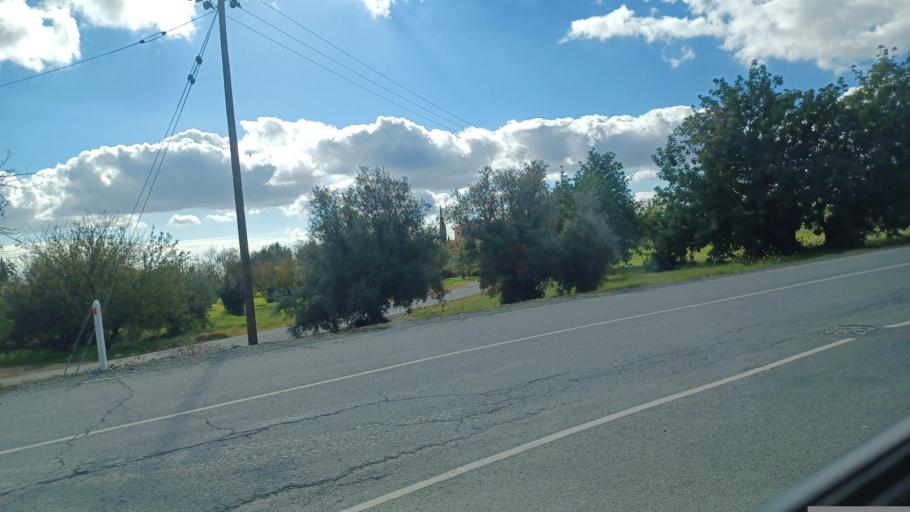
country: CY
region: Limassol
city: Pano Polemidia
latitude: 34.7841
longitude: 32.9728
